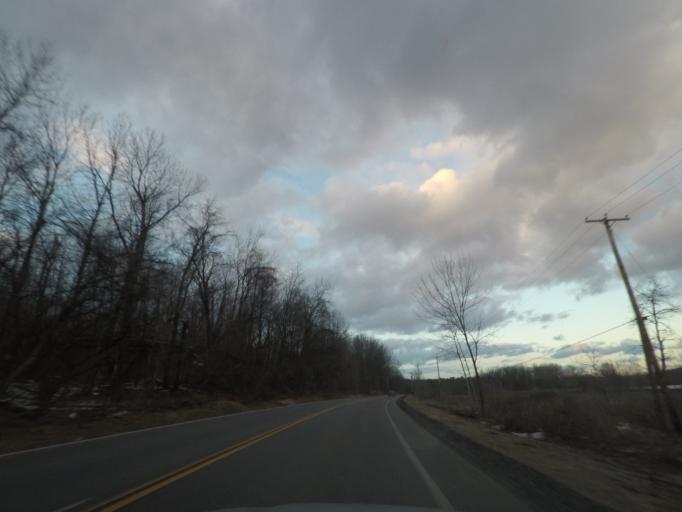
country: US
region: New York
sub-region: Montgomery County
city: Fonda
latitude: 42.9354
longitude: -74.4194
